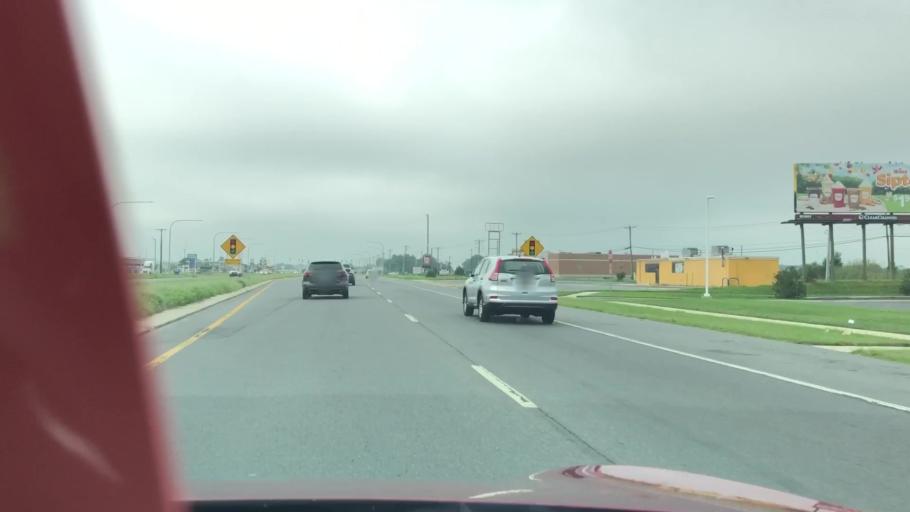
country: US
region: Delaware
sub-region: Sussex County
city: Bridgeville
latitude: 38.7261
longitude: -75.5908
